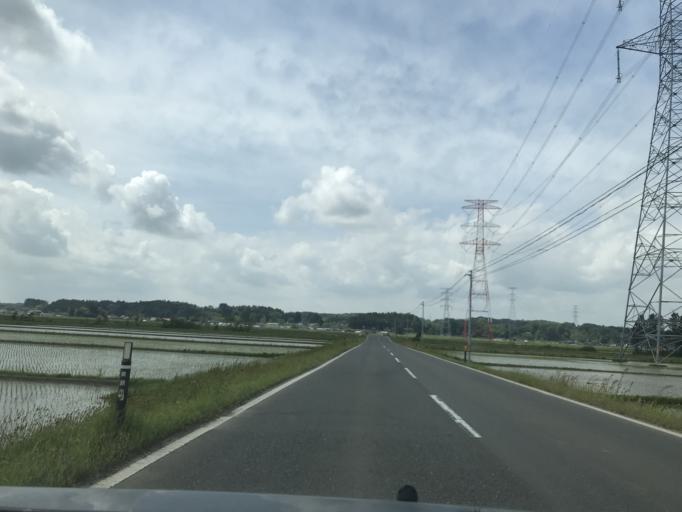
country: JP
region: Iwate
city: Ichinoseki
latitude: 38.7997
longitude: 141.0082
